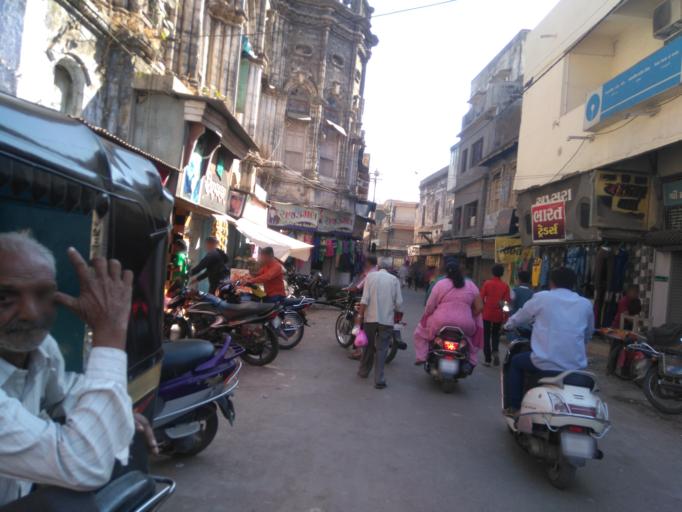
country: IN
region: Gujarat
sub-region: Junagadh
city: Junagadh
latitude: 21.5206
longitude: 70.4644
